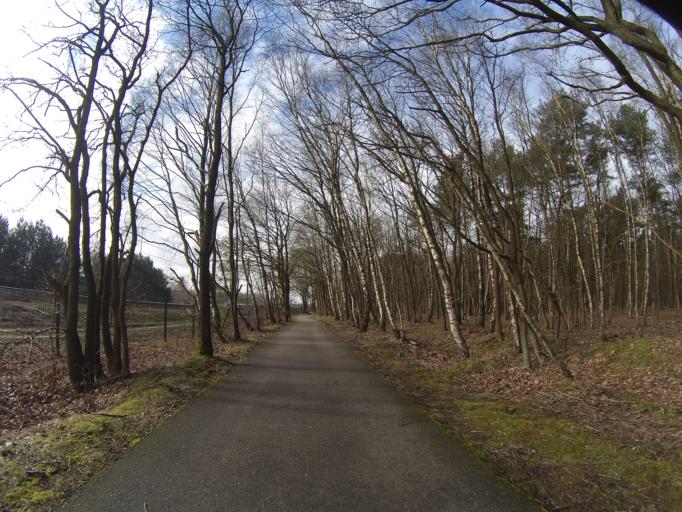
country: NL
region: Utrecht
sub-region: Gemeente Amersfoort
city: Amersfoort
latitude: 52.1469
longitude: 5.3414
